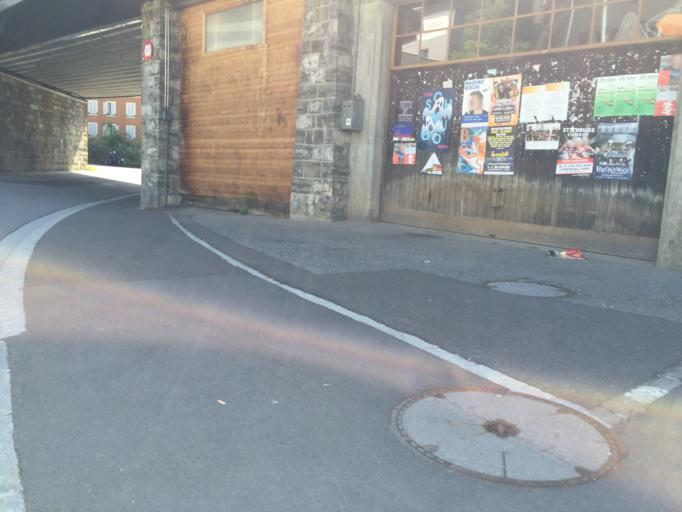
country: CH
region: Schwyz
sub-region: Bezirk Schwyz
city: Ingenbohl
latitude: 46.9953
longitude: 8.6081
